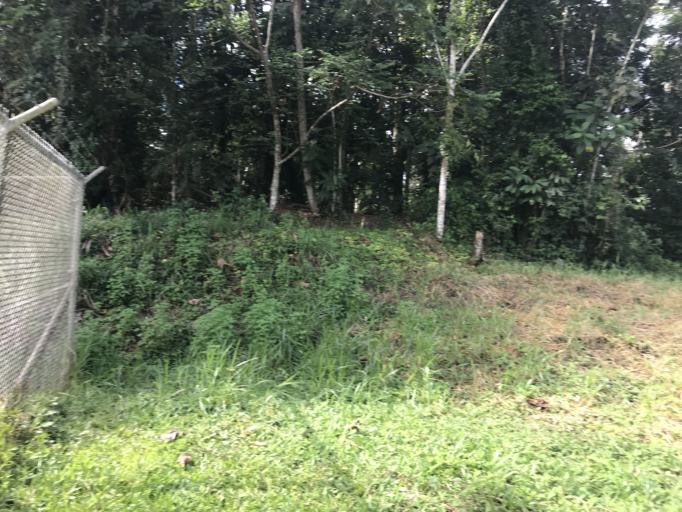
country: EC
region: Orellana
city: Puerto Francisco de Orellana
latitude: -0.6886
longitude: -76.4302
